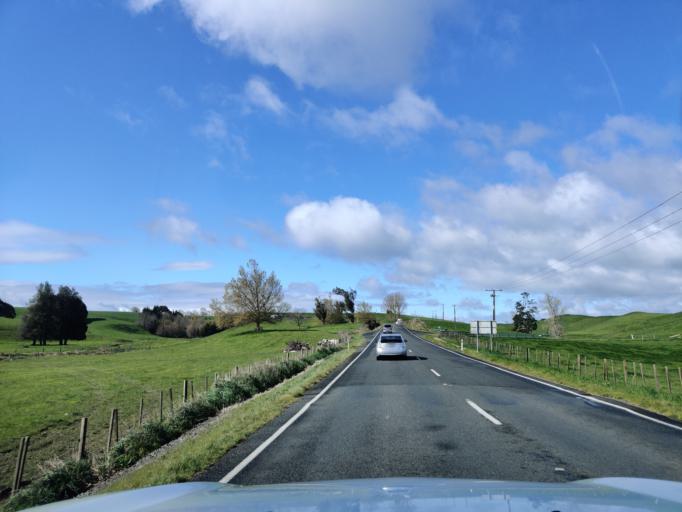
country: NZ
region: Waikato
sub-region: Otorohanga District
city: Otorohanga
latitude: -38.0899
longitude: 175.1822
